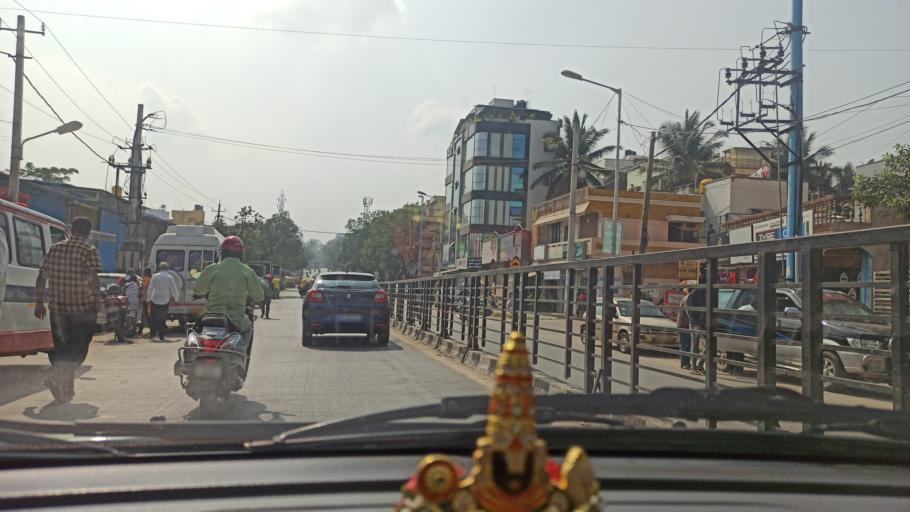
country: IN
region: Karnataka
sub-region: Bangalore Urban
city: Bangalore
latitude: 13.0136
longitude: 77.6436
